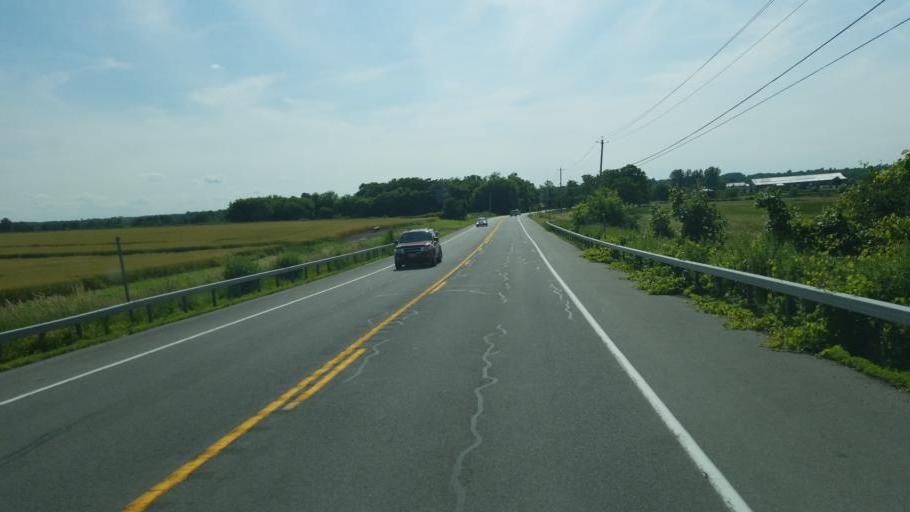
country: US
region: New York
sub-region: Livingston County
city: Lima
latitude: 42.9085
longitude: -77.5872
